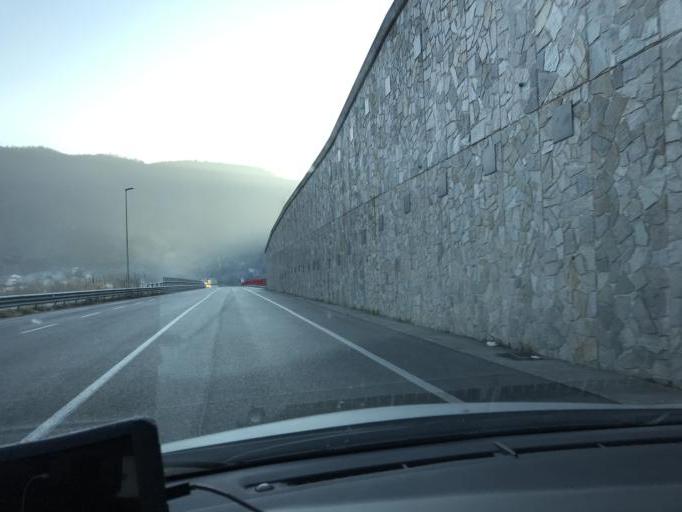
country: IT
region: Latium
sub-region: Provincia di Rieti
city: Cittaducale
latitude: 42.3519
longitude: 12.9572
